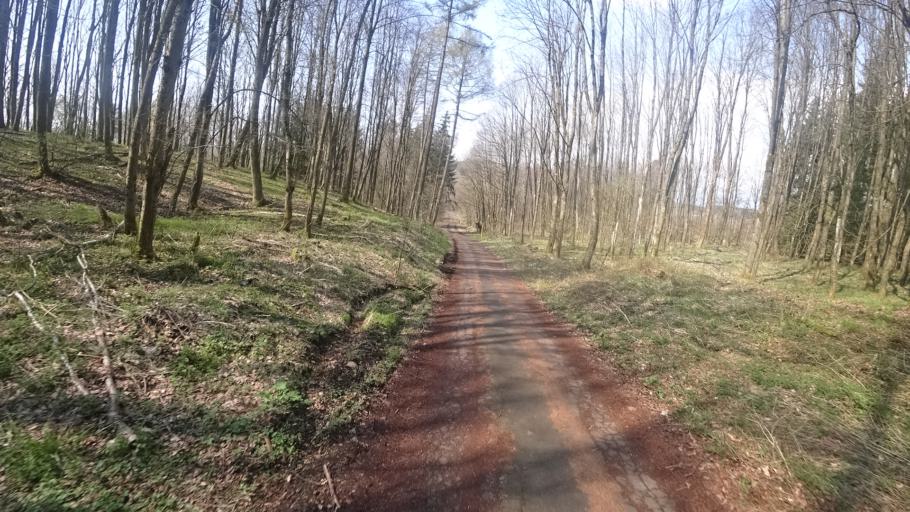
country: DE
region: Rheinland-Pfalz
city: Nauroth
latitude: 50.6980
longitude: 7.8629
